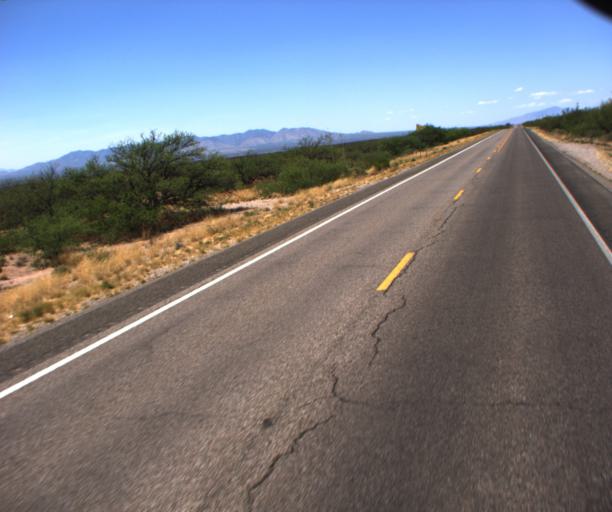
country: US
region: Arizona
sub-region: Cochise County
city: Tombstone
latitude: 31.7608
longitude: -110.1121
